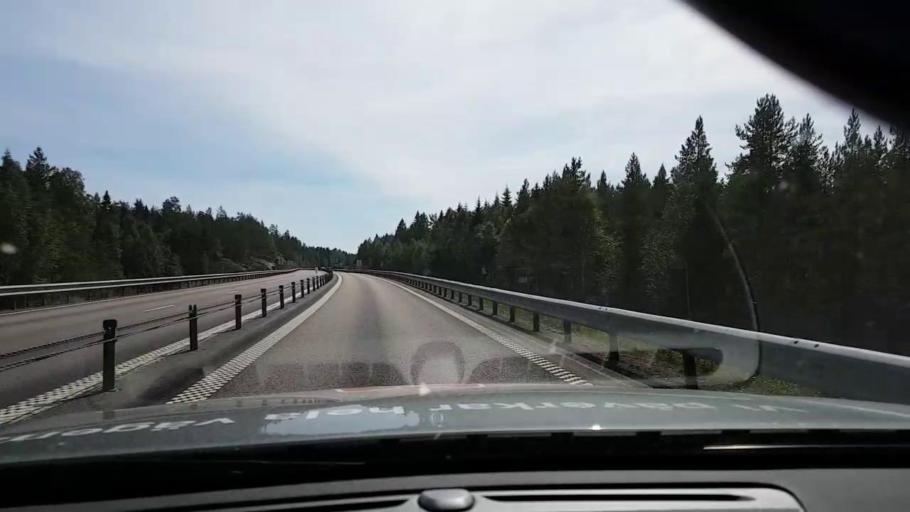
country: SE
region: Vaesternorrland
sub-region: OErnskoeldsviks Kommun
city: Husum
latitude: 63.3914
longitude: 19.1943
